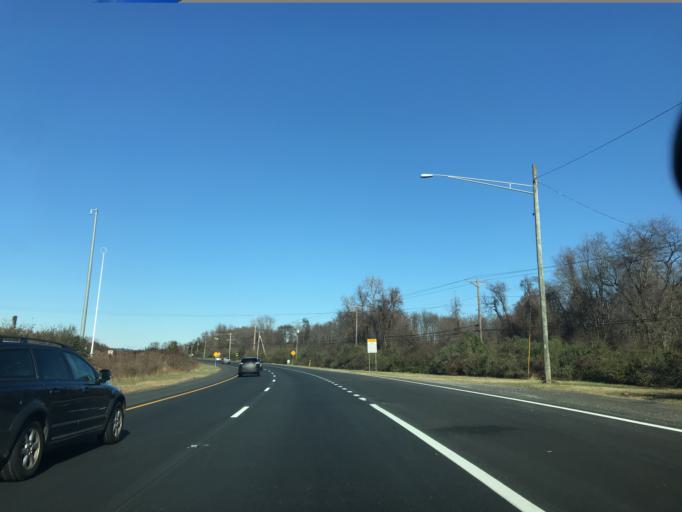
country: US
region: Delaware
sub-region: New Castle County
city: Glasgow
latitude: 39.5597
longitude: -75.7372
